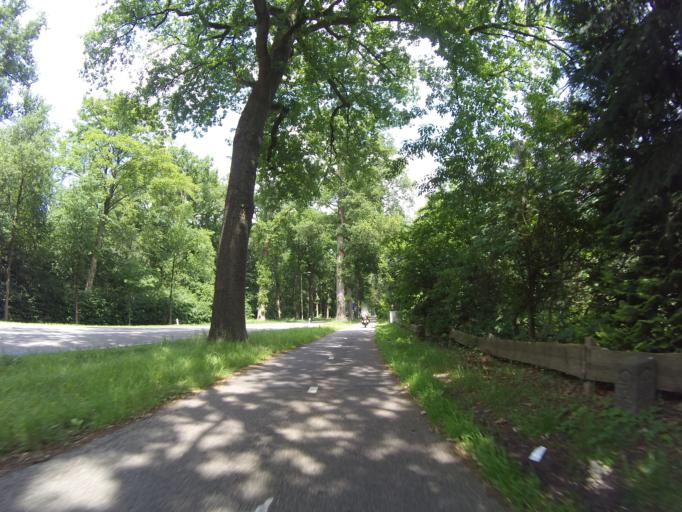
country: NL
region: Utrecht
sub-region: Gemeente Soest
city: Soest
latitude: 52.1741
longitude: 5.2472
